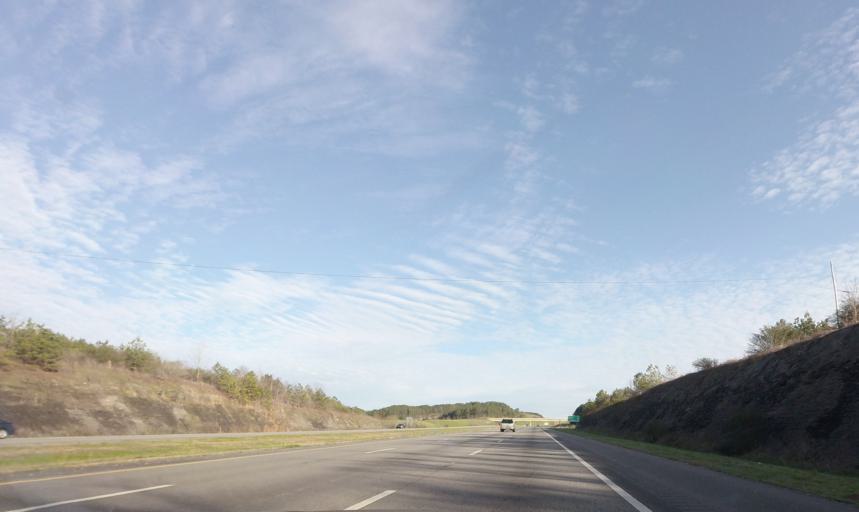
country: US
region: Alabama
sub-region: Walker County
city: Cordova
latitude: 33.7903
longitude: -87.2278
